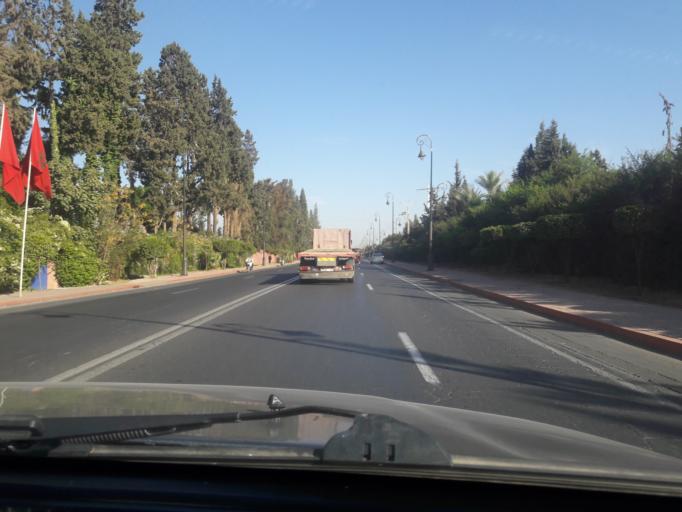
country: MA
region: Marrakech-Tensift-Al Haouz
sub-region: Marrakech
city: Marrakesh
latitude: 31.6484
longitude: -7.9618
